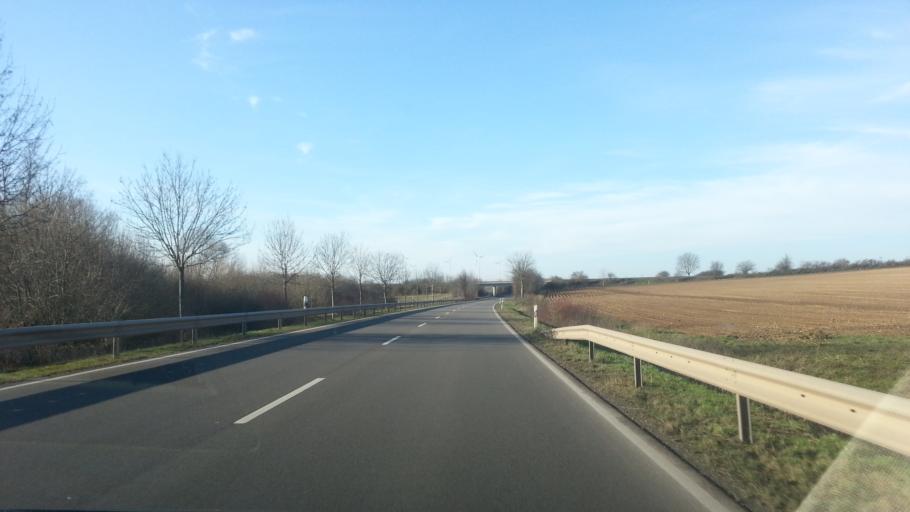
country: DE
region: Rheinland-Pfalz
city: Hohen-Sulzen
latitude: 49.6257
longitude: 8.2218
